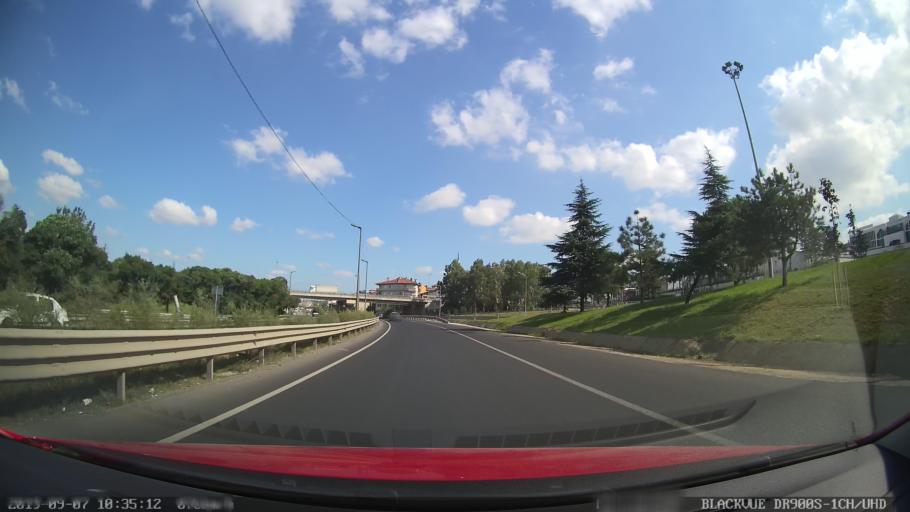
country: TR
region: Kocaeli
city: Darica
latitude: 40.8162
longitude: 29.3650
